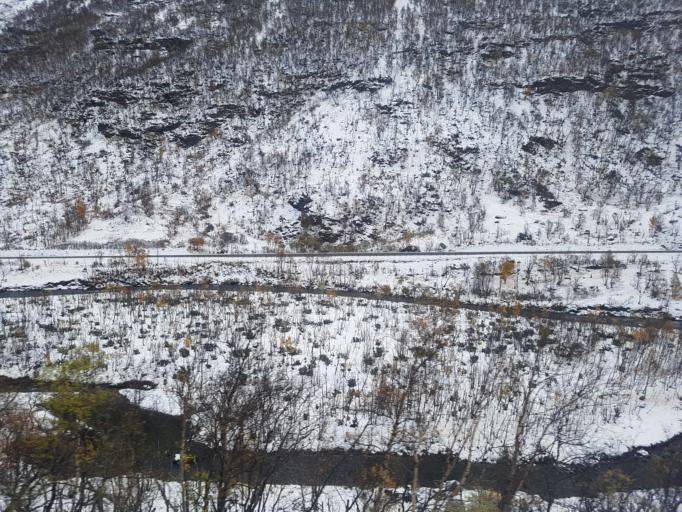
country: NO
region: Sor-Trondelag
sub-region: Oppdal
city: Oppdal
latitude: 62.3365
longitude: 9.6227
